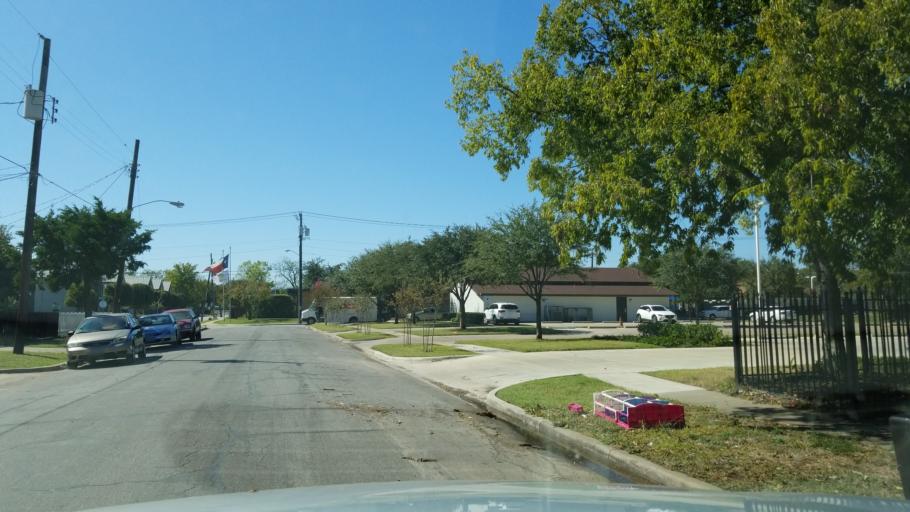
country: US
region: Texas
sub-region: Dallas County
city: Dallas
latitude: 32.7873
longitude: -96.7586
